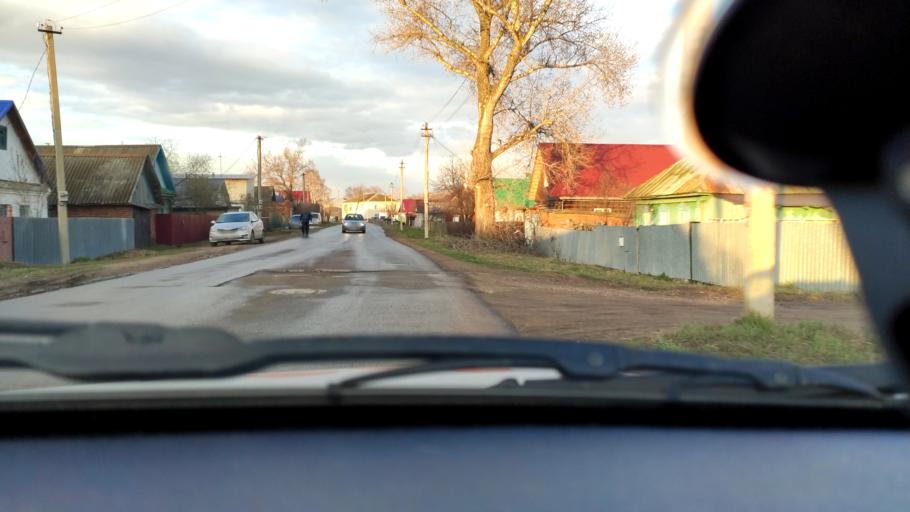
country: RU
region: Bashkortostan
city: Iglino
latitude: 54.7627
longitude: 56.2313
